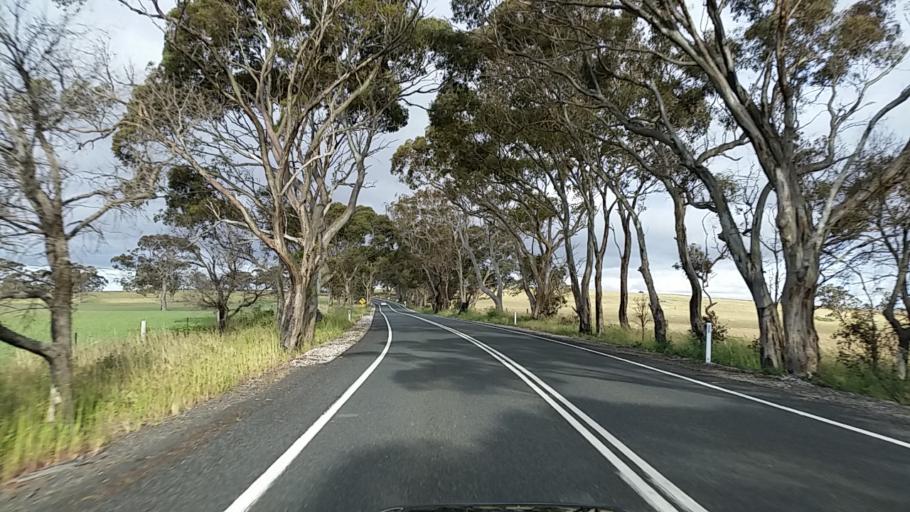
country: AU
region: South Australia
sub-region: Barossa
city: Angaston
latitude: -34.5641
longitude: 139.1810
